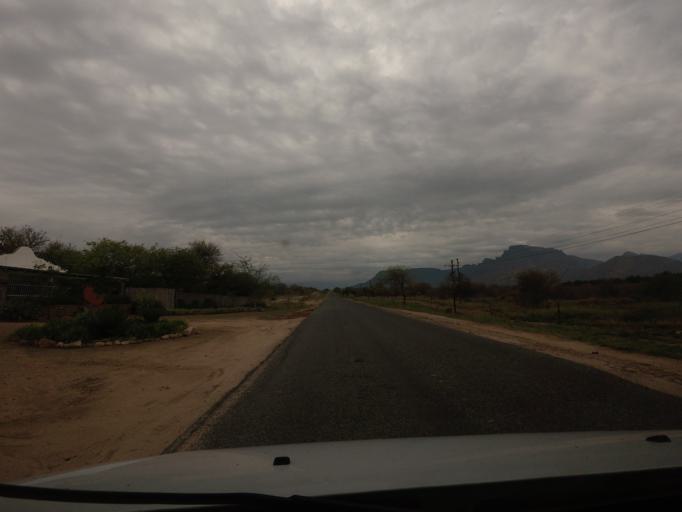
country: ZA
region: Limpopo
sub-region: Mopani District Municipality
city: Hoedspruit
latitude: -24.4571
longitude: 30.8667
